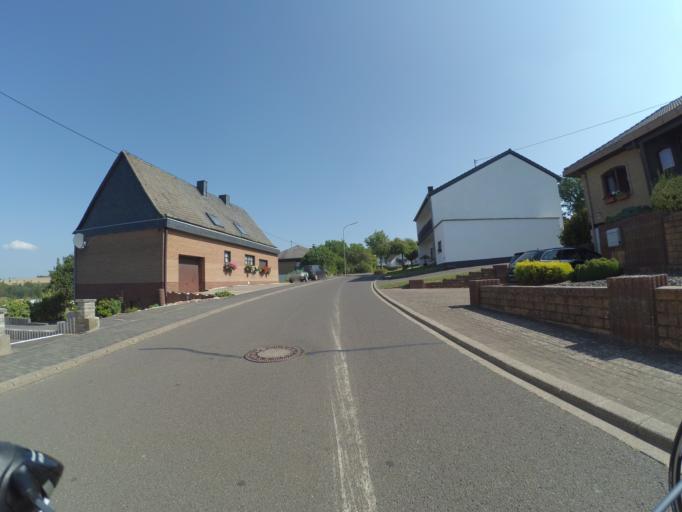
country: DE
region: Rheinland-Pfalz
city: Rorodt
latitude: 49.7700
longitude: 7.0882
